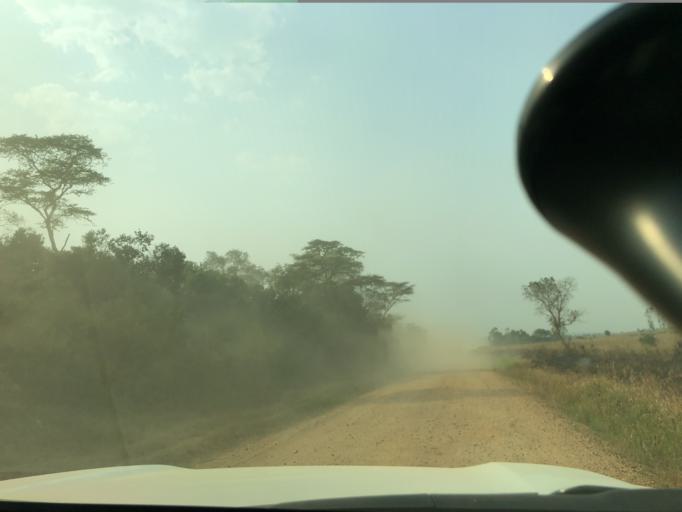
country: CD
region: Nord Kivu
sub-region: North Kivu
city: Butembo
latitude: 0.0872
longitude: 29.6435
